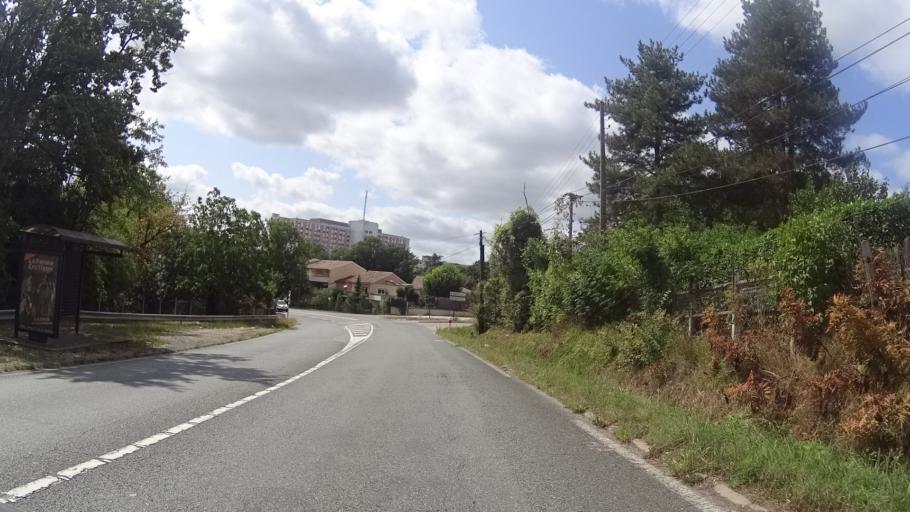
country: FR
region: Aquitaine
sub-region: Departement du Lot-et-Garonne
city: Agen
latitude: 44.2200
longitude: 0.6376
